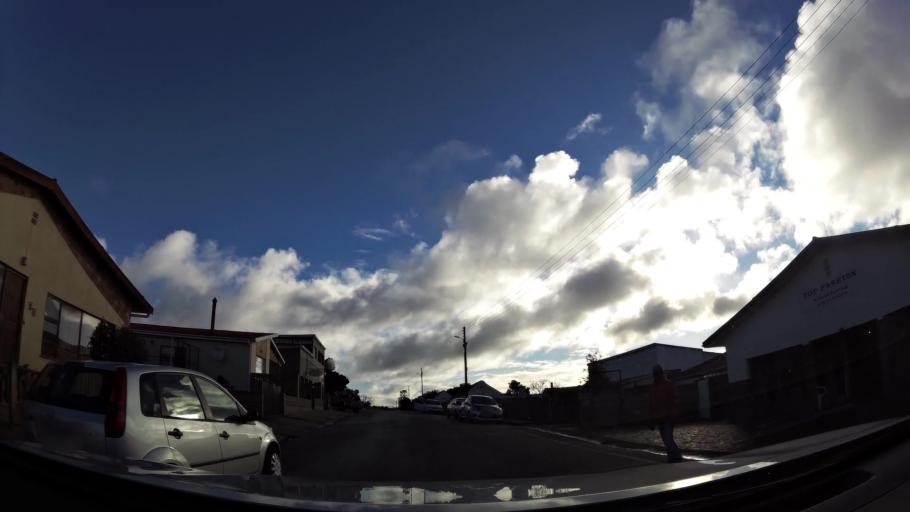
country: ZA
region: Western Cape
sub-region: Eden District Municipality
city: Riversdale
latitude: -34.2033
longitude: 21.5831
